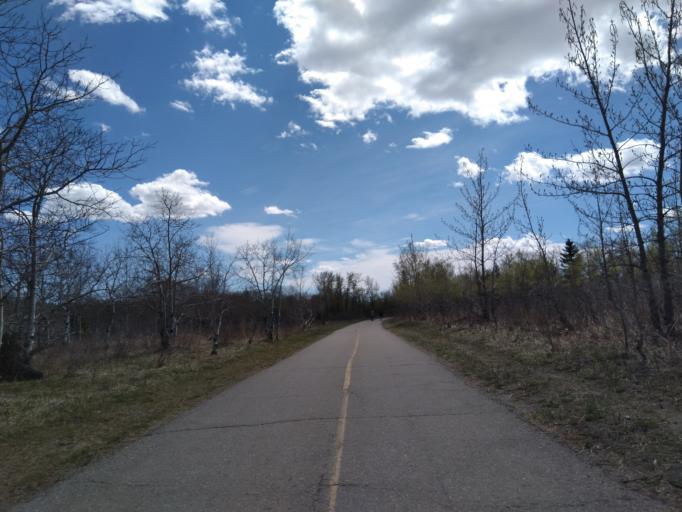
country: CA
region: Alberta
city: Calgary
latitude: 51.0920
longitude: -114.1818
